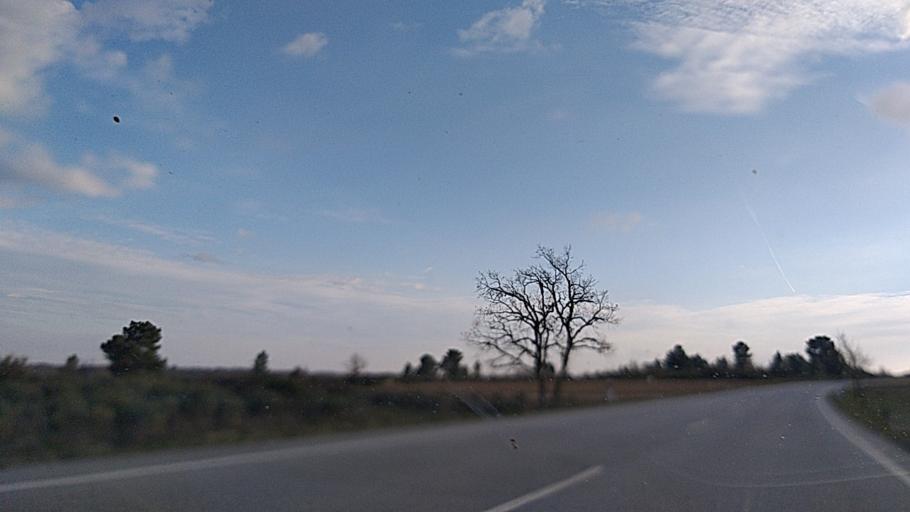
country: ES
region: Castille and Leon
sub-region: Provincia de Salamanca
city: Fuentes de Onoro
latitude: 40.6285
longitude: -6.9735
